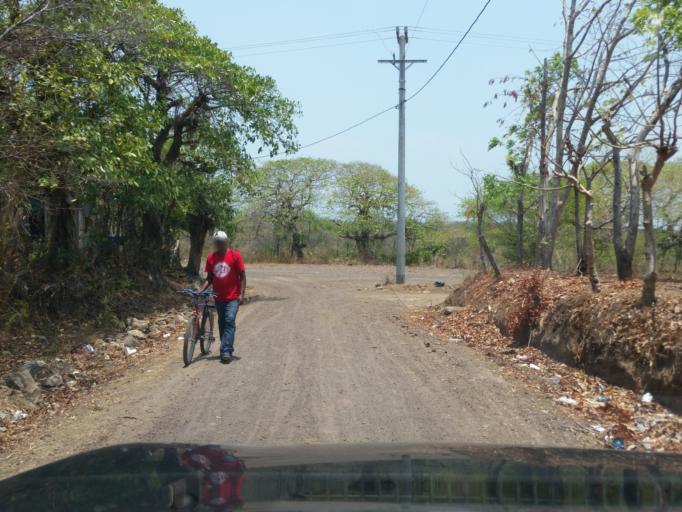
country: NI
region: Granada
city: Granada
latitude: 11.9081
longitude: -85.9459
